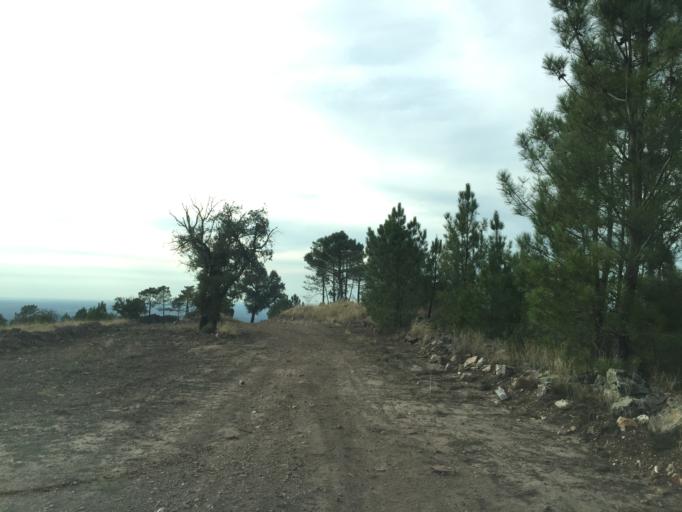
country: PT
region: Portalegre
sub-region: Portalegre
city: Reguengo
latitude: 39.3146
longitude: -7.3632
